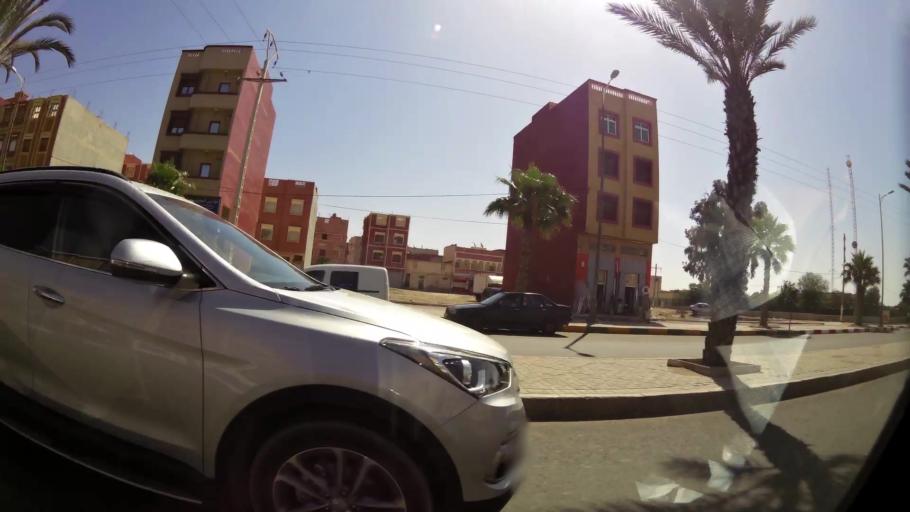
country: MA
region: Souss-Massa-Draa
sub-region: Inezgane-Ait Mellou
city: Inezgane
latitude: 30.3321
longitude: -9.5039
